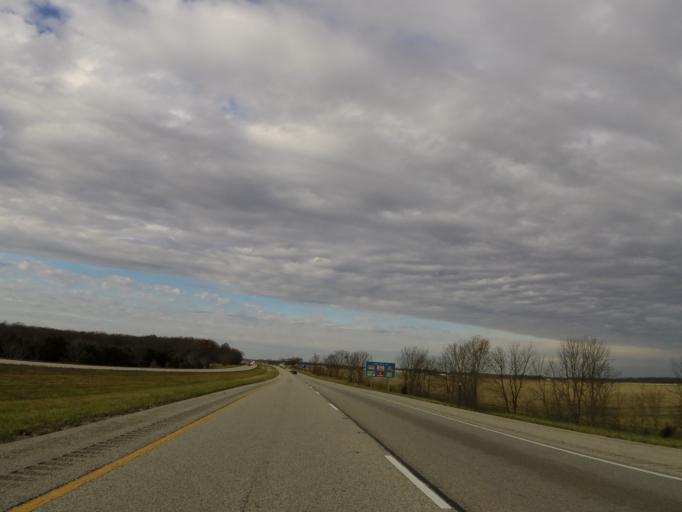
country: US
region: Illinois
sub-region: Washington County
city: Nashville
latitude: 38.3908
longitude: -89.3389
